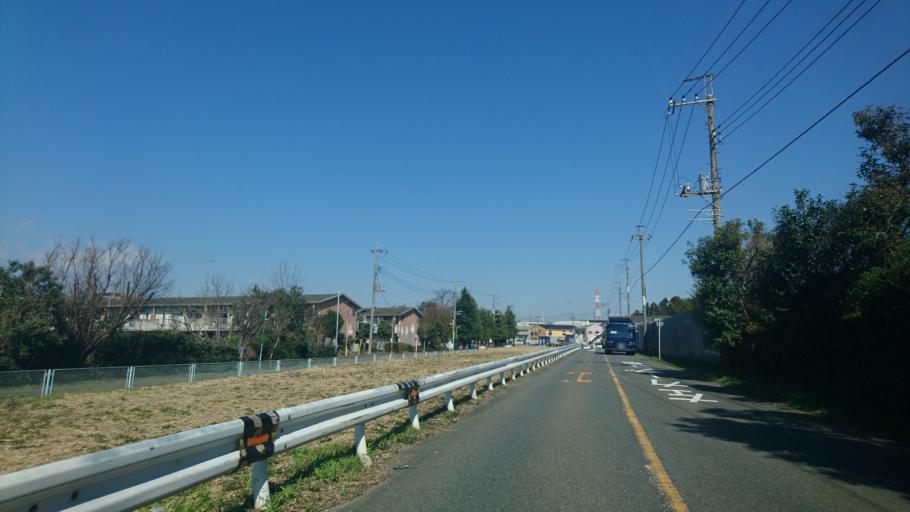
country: JP
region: Kanagawa
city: Fujisawa
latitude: 35.3975
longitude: 139.4477
